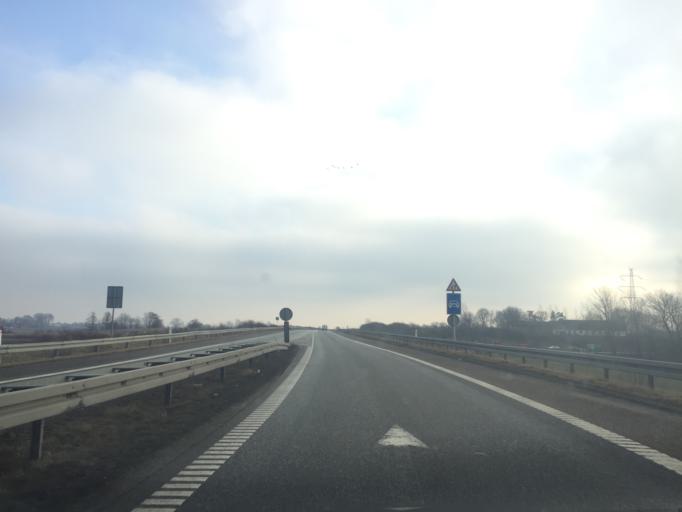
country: DK
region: Capital Region
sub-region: Hoje-Taastrup Kommune
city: Flong
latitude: 55.6639
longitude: 12.2332
